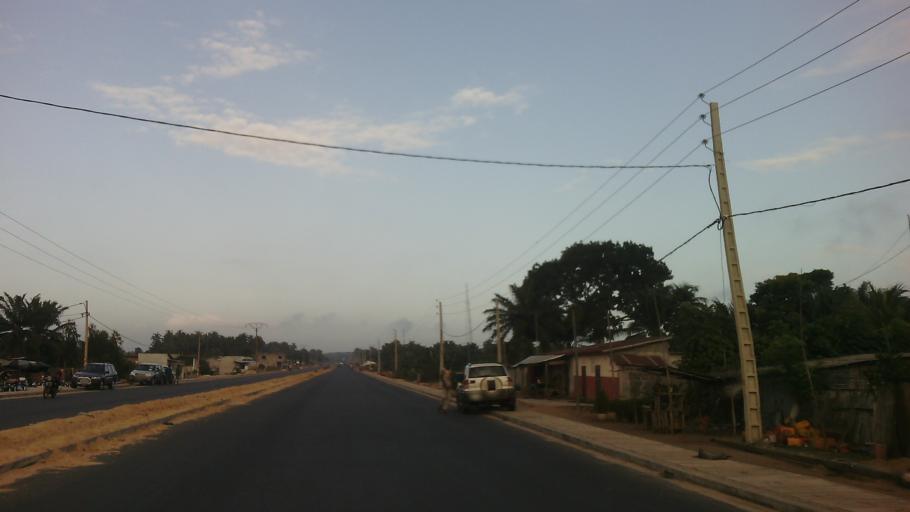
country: BJ
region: Atlantique
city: Hevie
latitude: 6.3831
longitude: 2.1843
